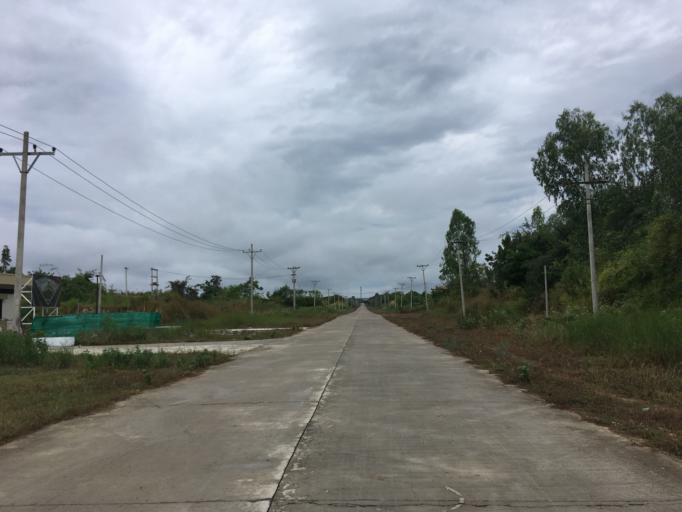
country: MM
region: Mandalay
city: Nay Pyi Taw
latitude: 19.6964
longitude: 96.1212
